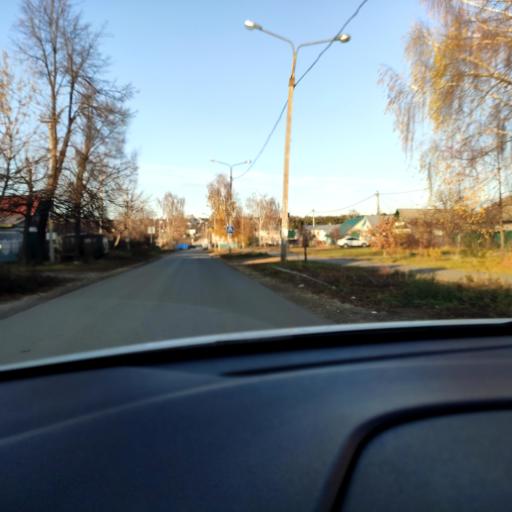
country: RU
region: Tatarstan
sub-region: Gorod Kazan'
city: Kazan
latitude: 55.8800
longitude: 49.0700
